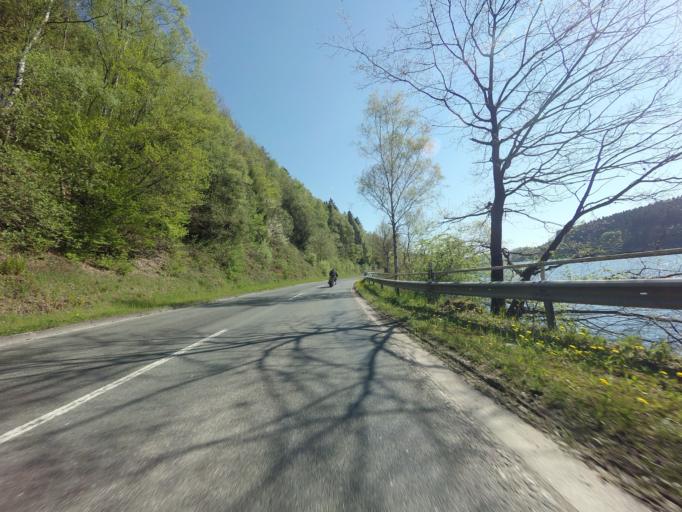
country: DE
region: North Rhine-Westphalia
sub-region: Regierungsbezirk Arnsberg
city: Olpe
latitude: 51.0924
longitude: 7.8270
